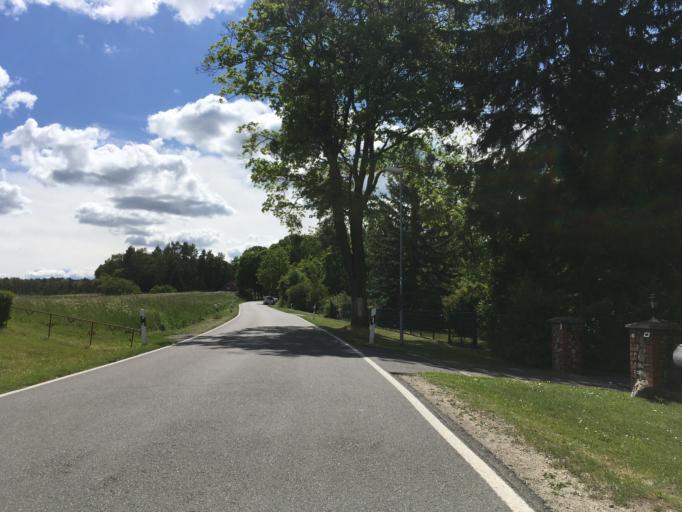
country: DE
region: Brandenburg
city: Protzel
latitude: 52.6779
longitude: 14.0022
